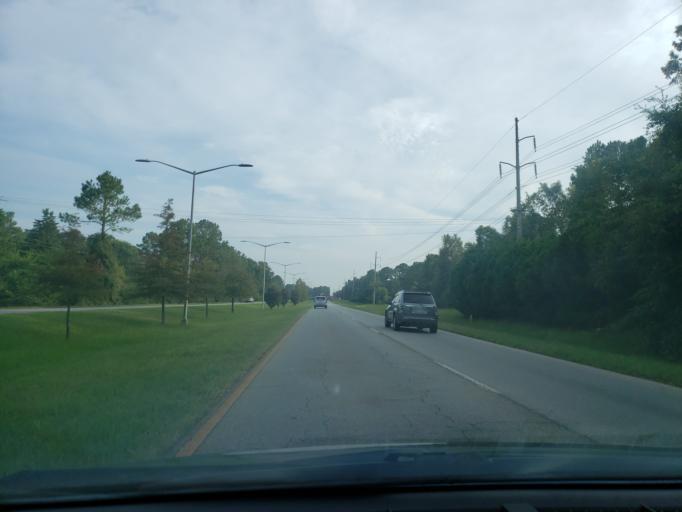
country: US
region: Georgia
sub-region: Dougherty County
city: Albany
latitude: 31.5946
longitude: -84.2194
